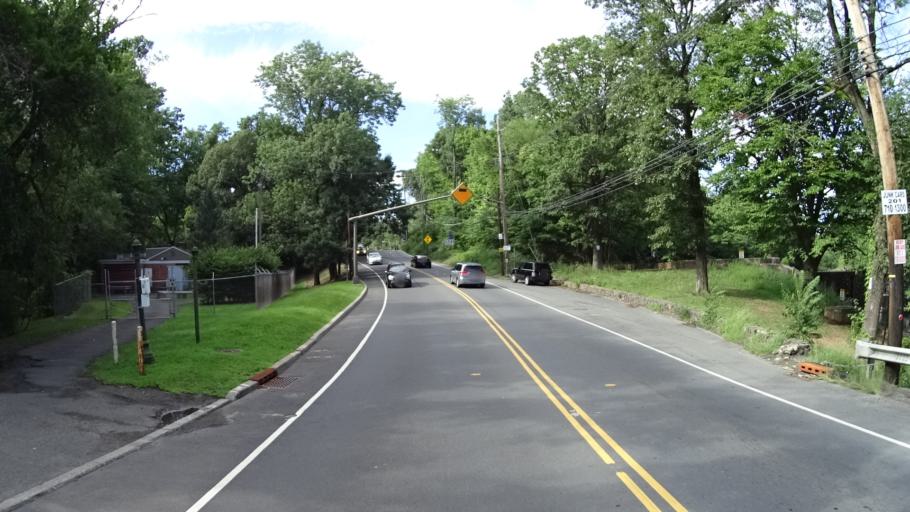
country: US
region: New Jersey
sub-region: Union County
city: Scotch Plains
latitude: 40.6670
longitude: -74.4037
